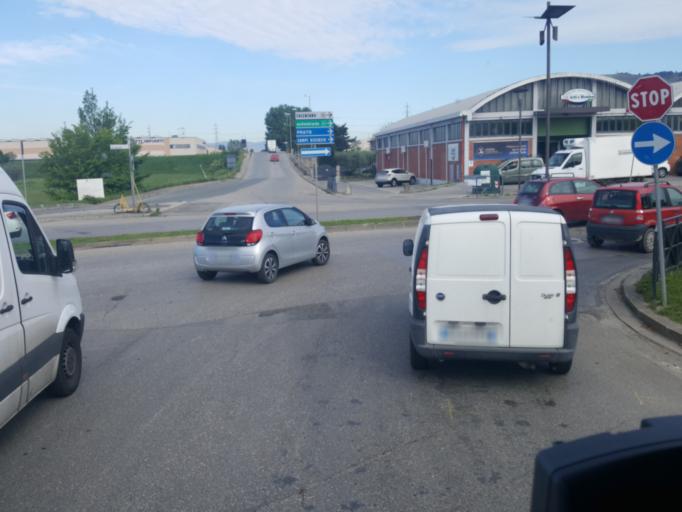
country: IT
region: Tuscany
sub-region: Province of Florence
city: Calenzano
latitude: 43.8443
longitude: 11.1589
